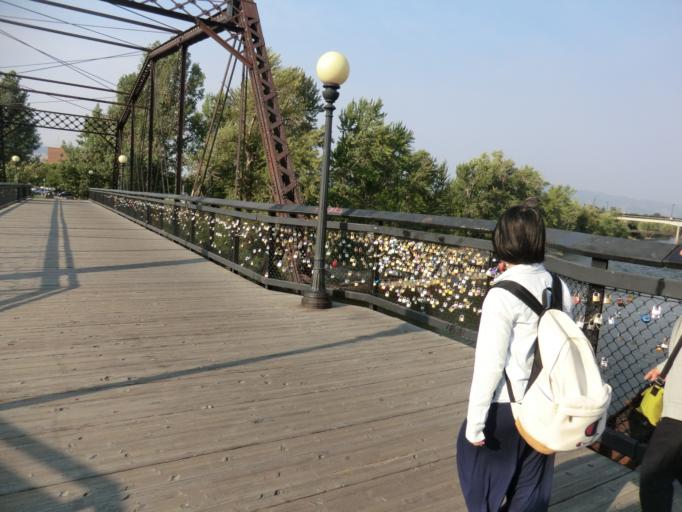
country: US
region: Montana
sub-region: Missoula County
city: Missoula
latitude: 46.8674
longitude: -113.9836
